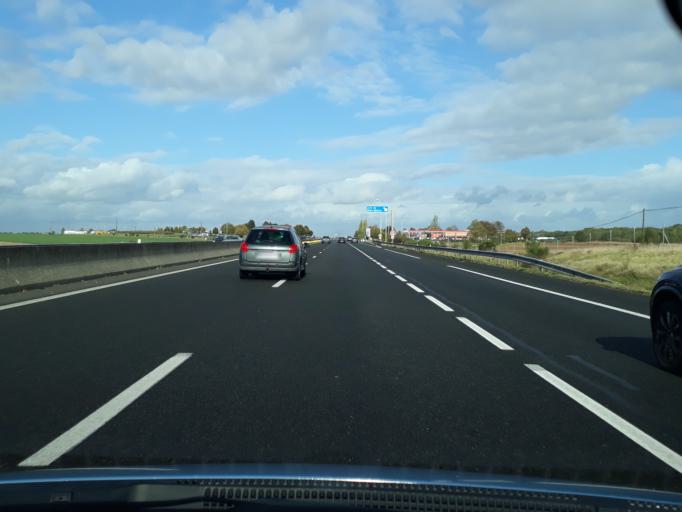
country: FR
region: Centre
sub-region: Departement du Loir-et-Cher
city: La Chaussee-Saint-Victor
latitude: 47.6597
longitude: 1.3832
